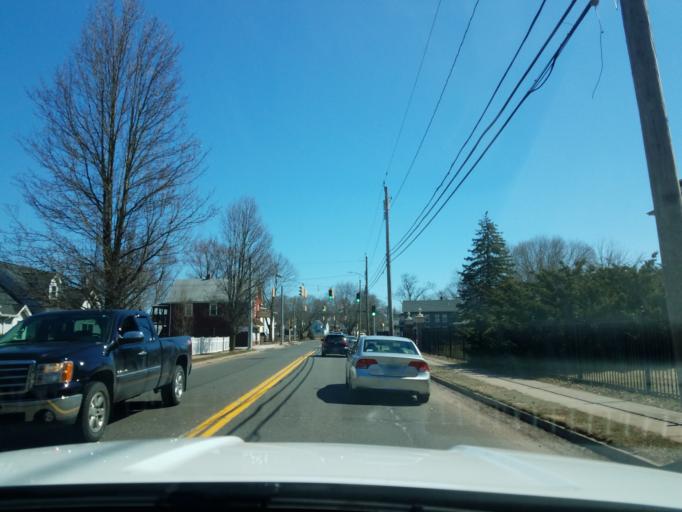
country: US
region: Connecticut
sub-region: New Haven County
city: Wallingford
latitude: 41.4571
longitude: -72.8341
